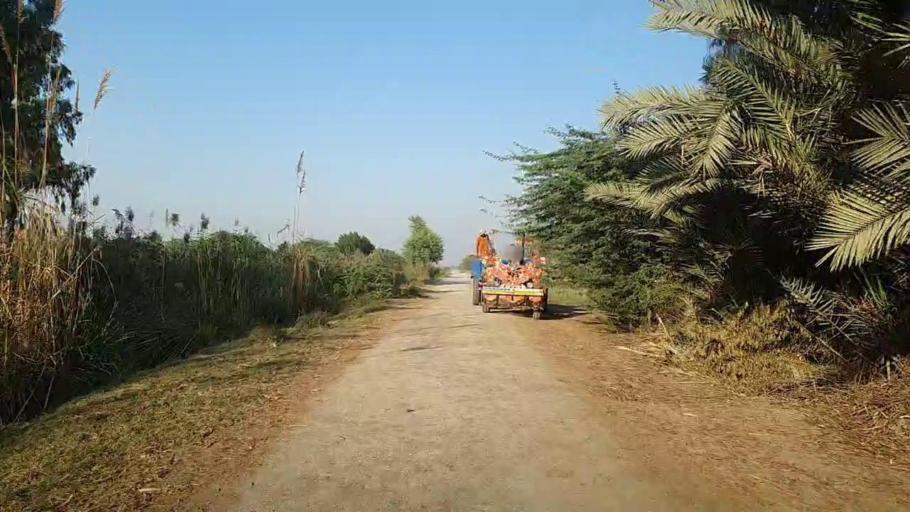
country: PK
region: Sindh
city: Ranipur
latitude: 27.2501
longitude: 68.5067
